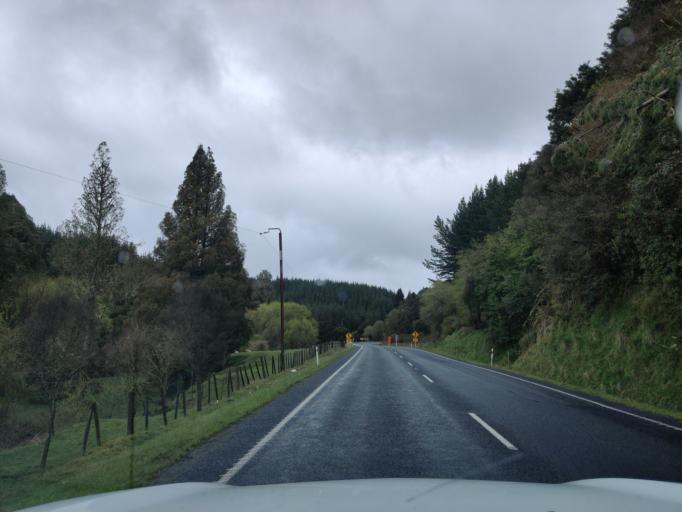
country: NZ
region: Waikato
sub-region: Otorohanga District
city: Otorohanga
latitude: -38.6553
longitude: 175.2082
